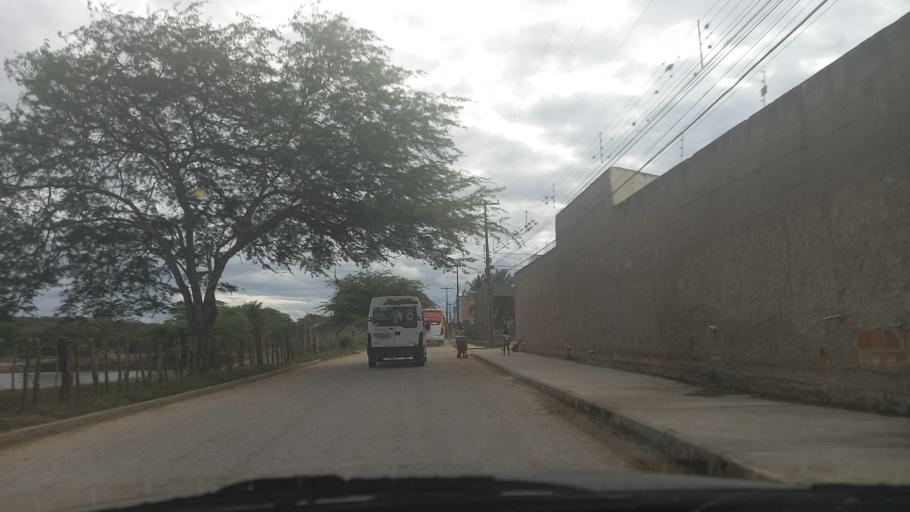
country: BR
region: Pernambuco
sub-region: Caruaru
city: Caruaru
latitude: -8.2984
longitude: -36.0317
